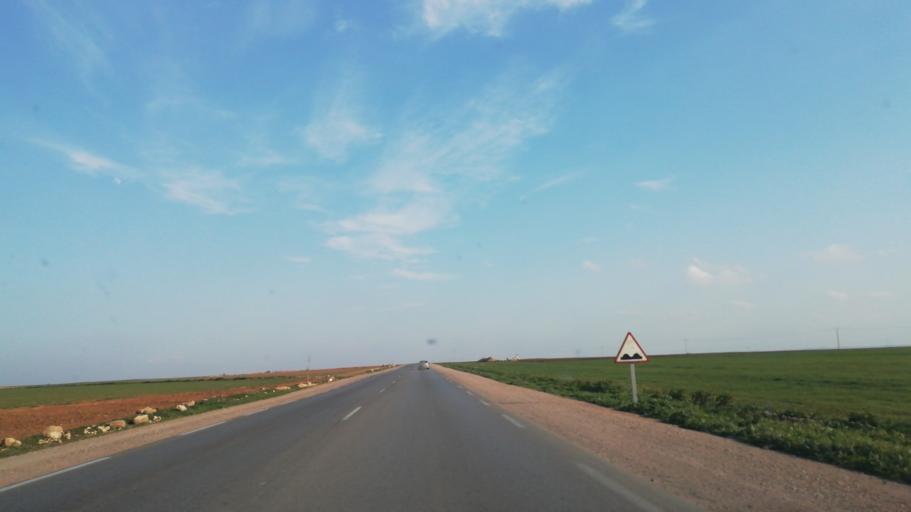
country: DZ
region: Relizane
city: Relizane
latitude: 35.8949
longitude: 0.6042
